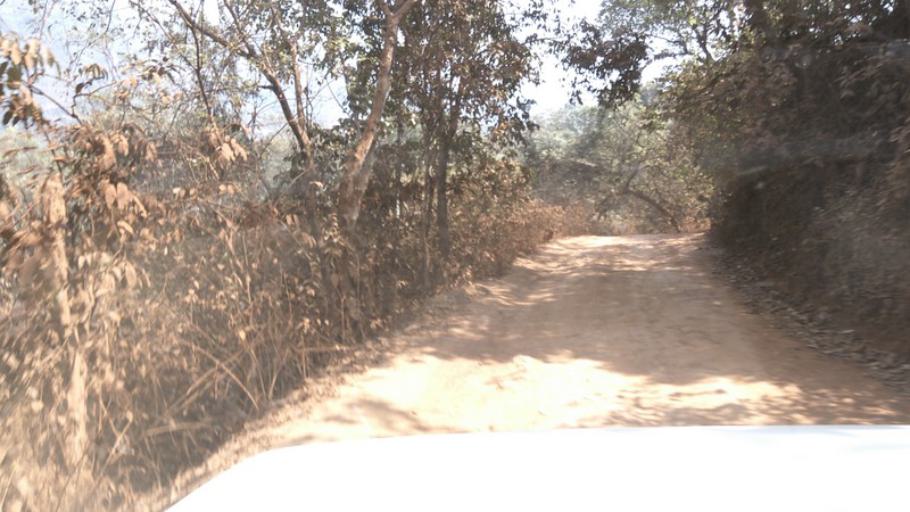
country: IN
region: Goa
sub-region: South Goa
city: Sanguem
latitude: 15.3114
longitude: 74.2988
